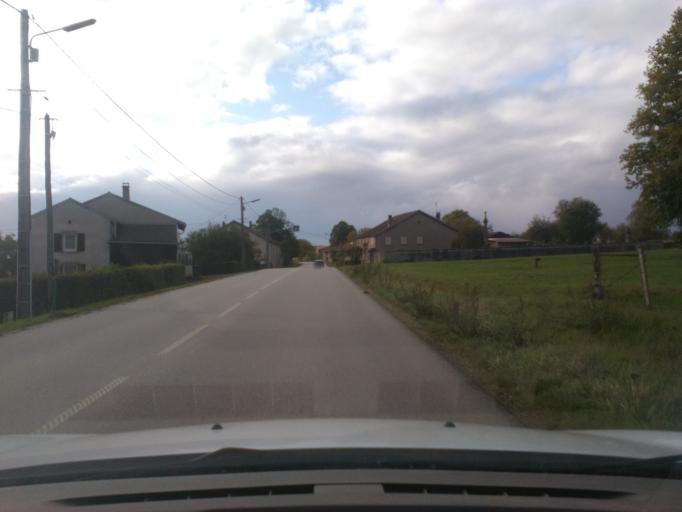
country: FR
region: Lorraine
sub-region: Departement des Vosges
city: Aydoilles
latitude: 48.2472
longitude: 6.6242
